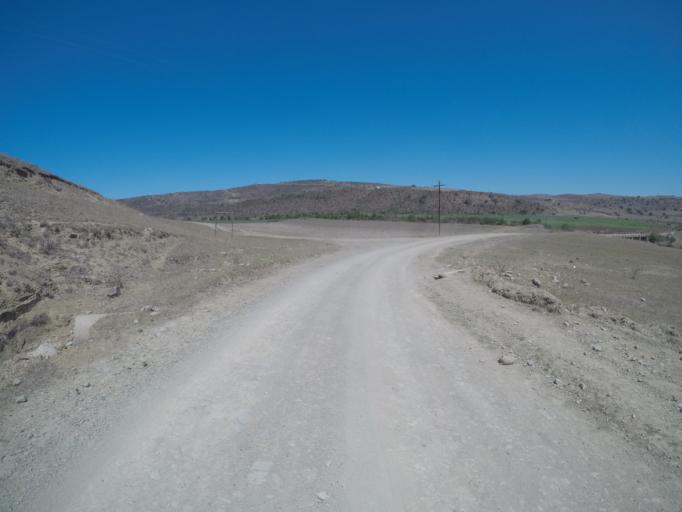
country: ZA
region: Eastern Cape
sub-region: OR Tambo District Municipality
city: Mthatha
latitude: -31.8684
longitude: 28.8724
